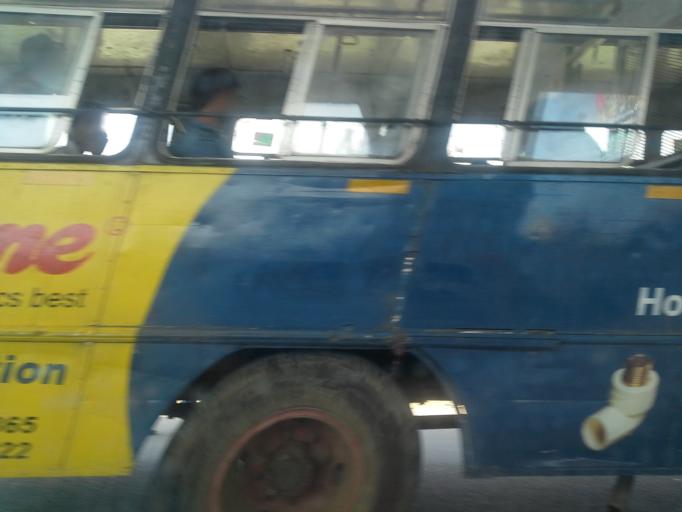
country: IN
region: Telangana
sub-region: Hyderabad
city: Hyderabad
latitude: 17.3630
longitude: 78.4280
